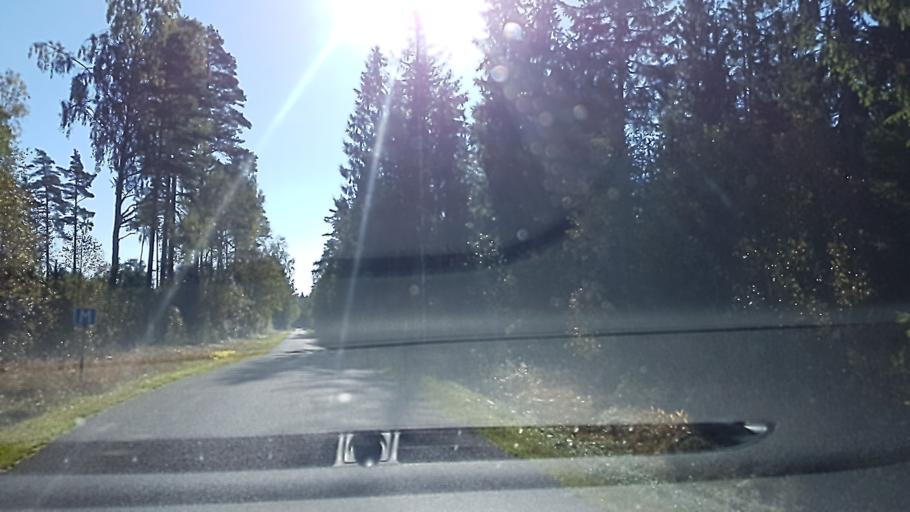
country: SE
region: Kronoberg
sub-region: Ljungby Kommun
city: Ljungby
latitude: 56.8060
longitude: 14.0280
